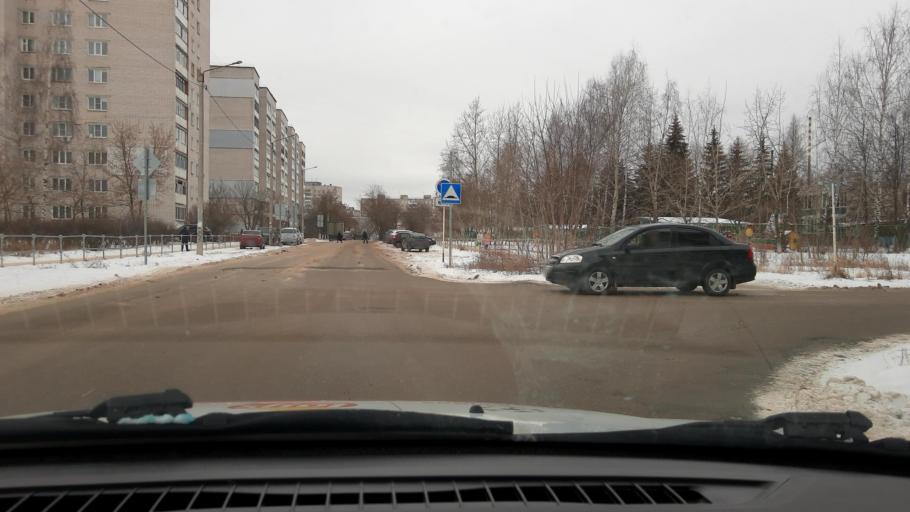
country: RU
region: Nizjnij Novgorod
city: Dzerzhinsk
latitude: 56.2299
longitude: 43.4054
